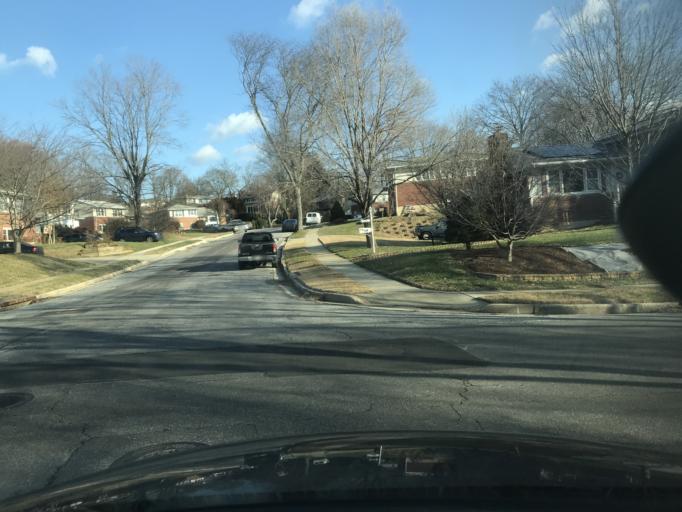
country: US
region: Maryland
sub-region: Baltimore County
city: Towson
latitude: 39.4036
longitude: -76.5862
